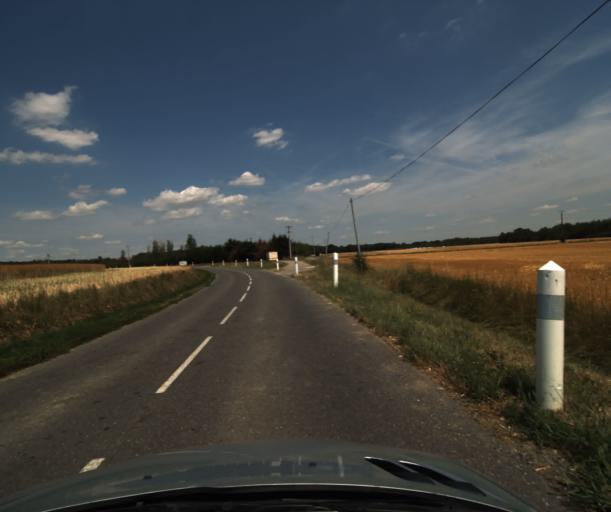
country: FR
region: Midi-Pyrenees
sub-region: Departement de la Haute-Garonne
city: Labastidette
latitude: 43.4841
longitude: 1.2169
